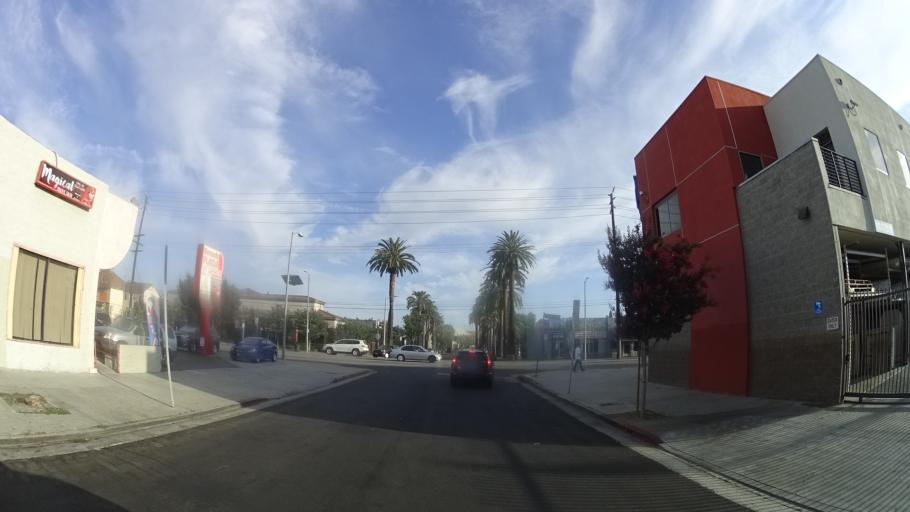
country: US
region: California
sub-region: Los Angeles County
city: Silver Lake
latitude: 34.0913
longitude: -118.2937
